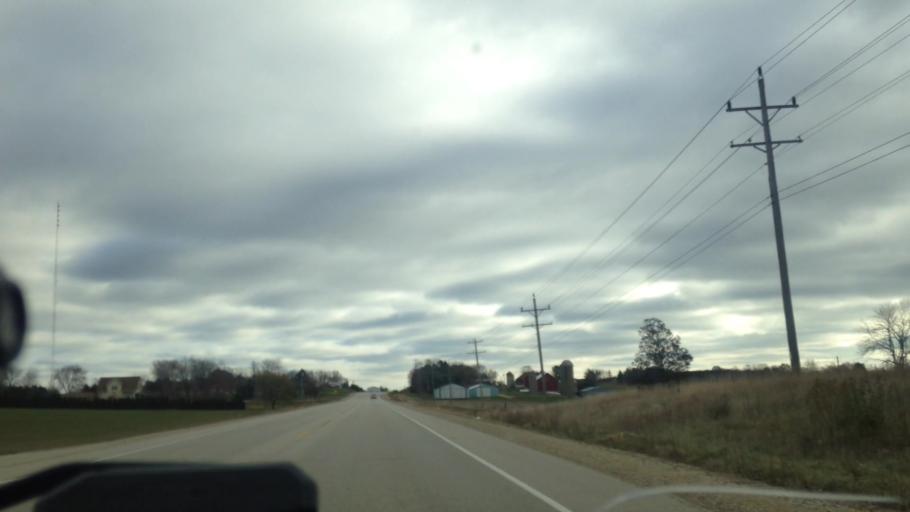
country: US
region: Wisconsin
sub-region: Washington County
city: Slinger
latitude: 43.4274
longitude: -88.3083
